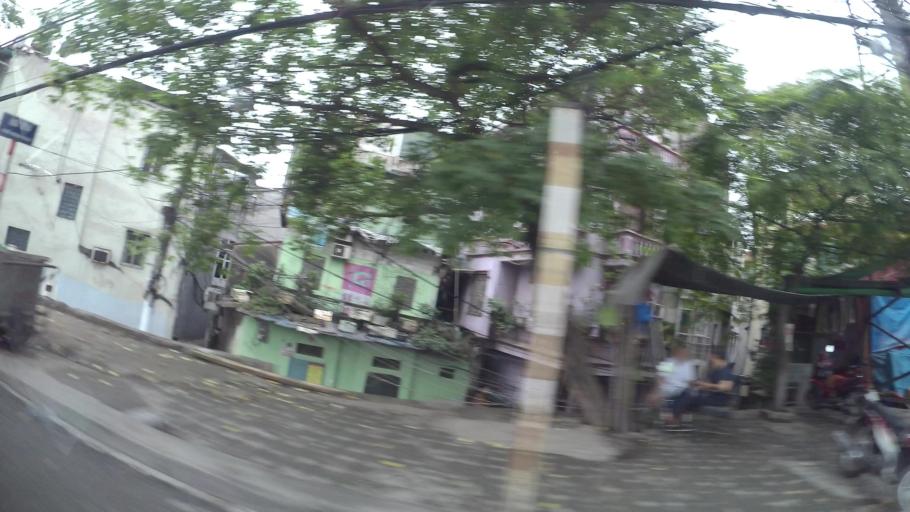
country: VN
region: Ha Noi
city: Hai BaTrung
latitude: 21.0053
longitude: 105.8688
